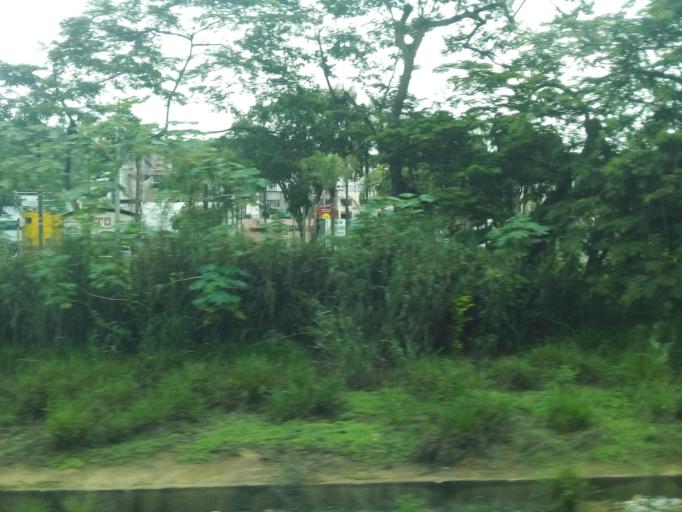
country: BR
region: Minas Gerais
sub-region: Ipatinga
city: Ipatinga
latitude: -19.5075
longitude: -42.5702
